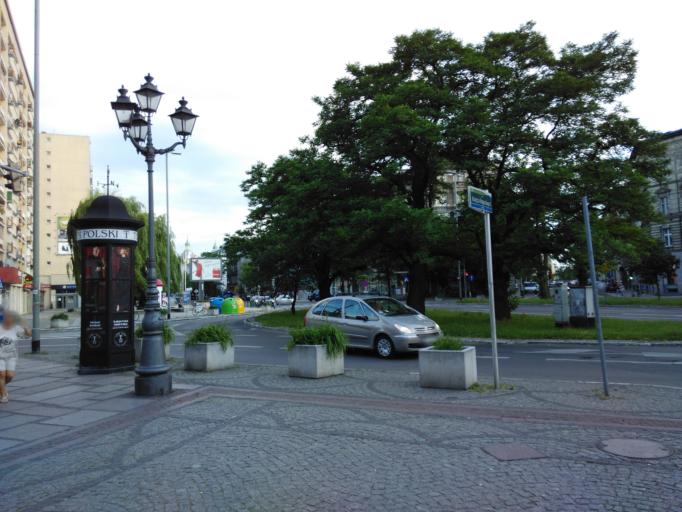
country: PL
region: West Pomeranian Voivodeship
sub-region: Szczecin
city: Szczecin
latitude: 53.4291
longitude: 14.5440
